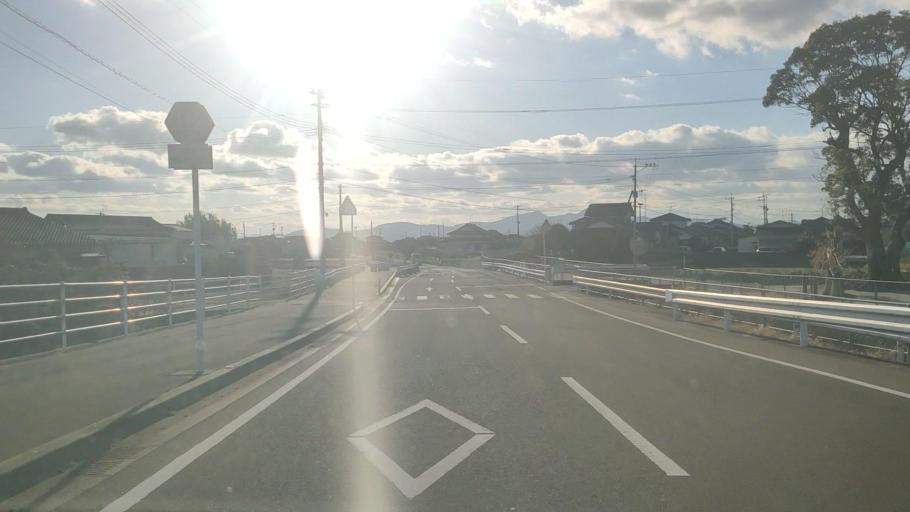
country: JP
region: Saga Prefecture
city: Saga-shi
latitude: 33.2966
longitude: 130.2440
